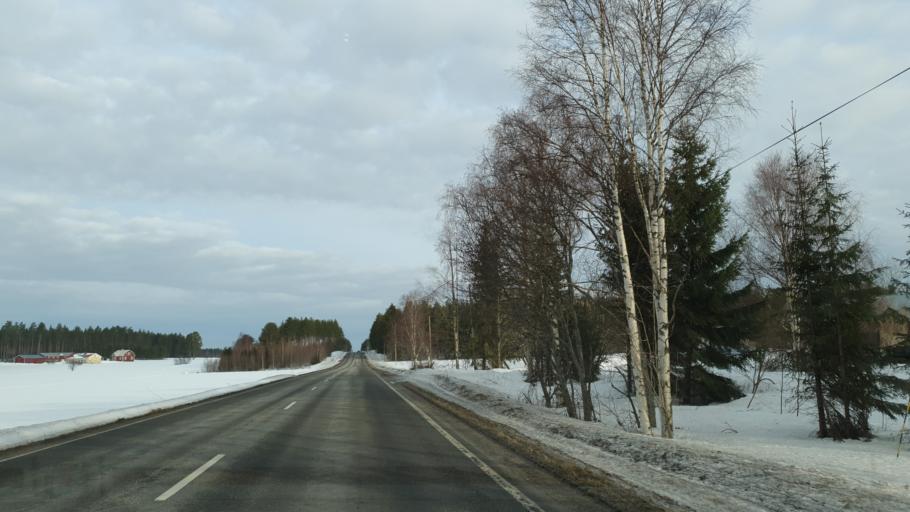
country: FI
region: Kainuu
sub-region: Kajaani
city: Vuokatti
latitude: 64.1774
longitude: 28.1959
